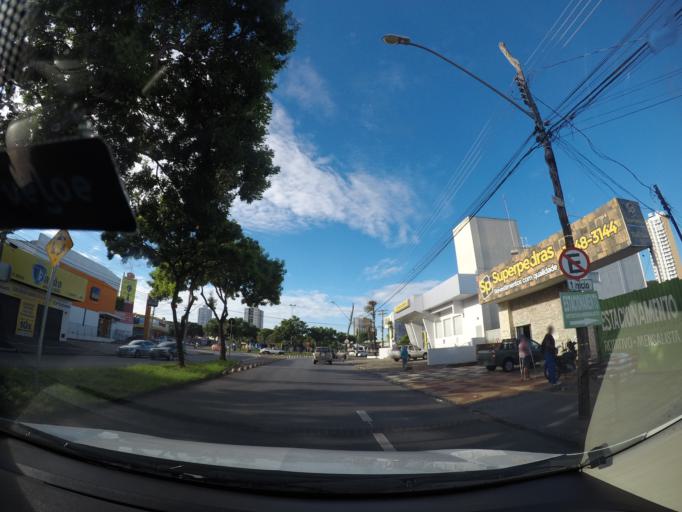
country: BR
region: Goias
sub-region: Goiania
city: Goiania
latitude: -16.7315
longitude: -49.2722
